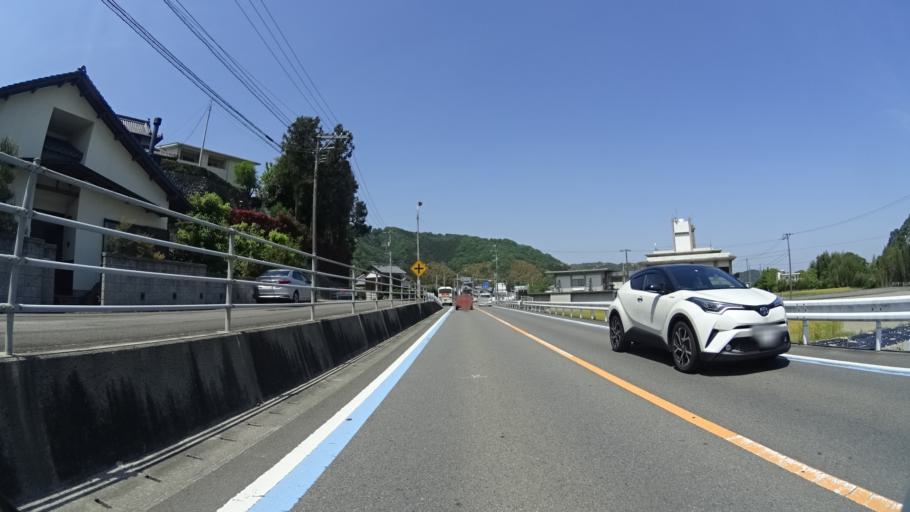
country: JP
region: Ehime
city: Hojo
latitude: 34.0183
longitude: 132.9407
